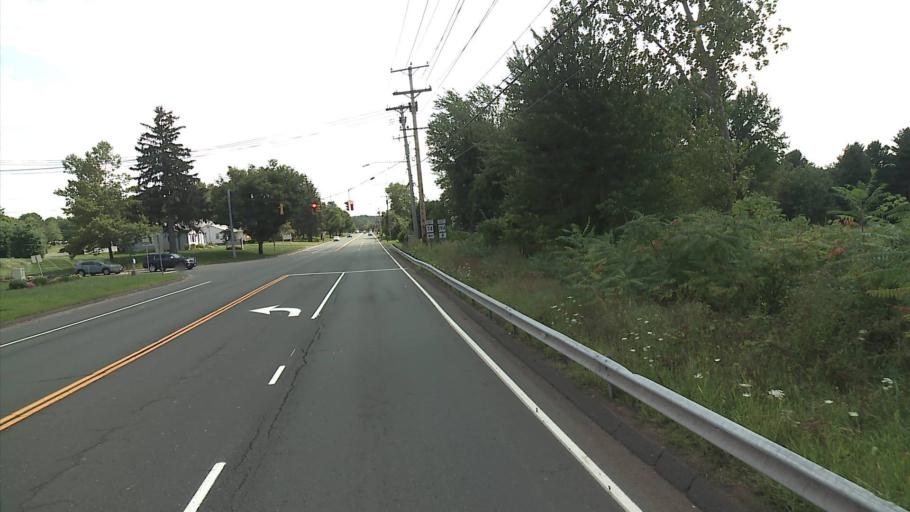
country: US
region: Connecticut
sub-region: Hartford County
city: Manchester
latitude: 41.8312
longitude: -72.5553
